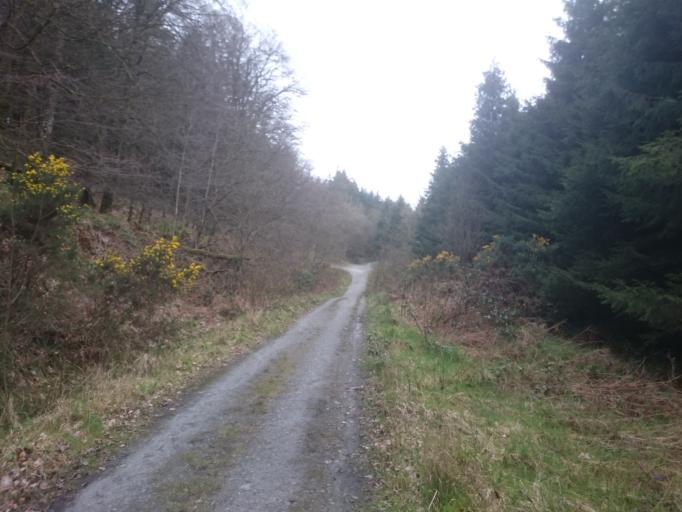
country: IE
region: Leinster
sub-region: Kilkenny
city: Callan
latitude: 52.6602
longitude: -7.5383
